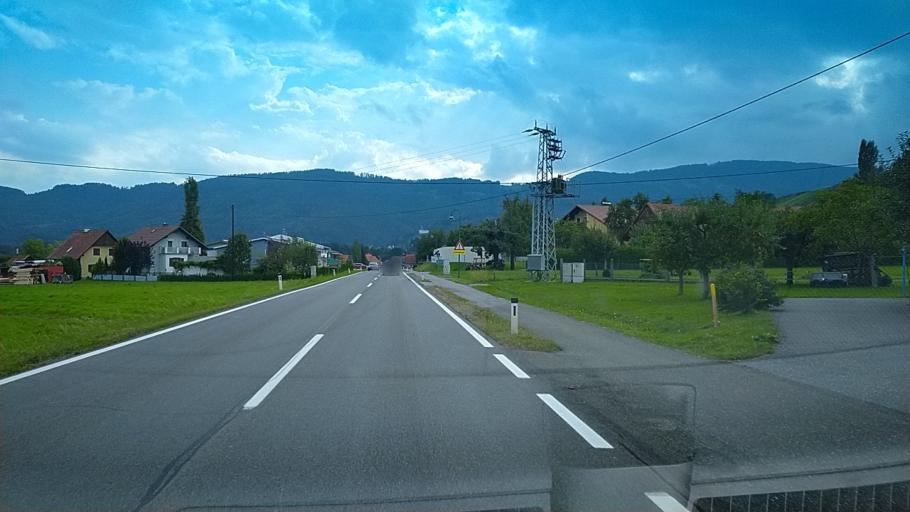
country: AT
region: Styria
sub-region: Politischer Bezirk Deutschlandsberg
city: Schwanberg
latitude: 46.7717
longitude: 15.2131
